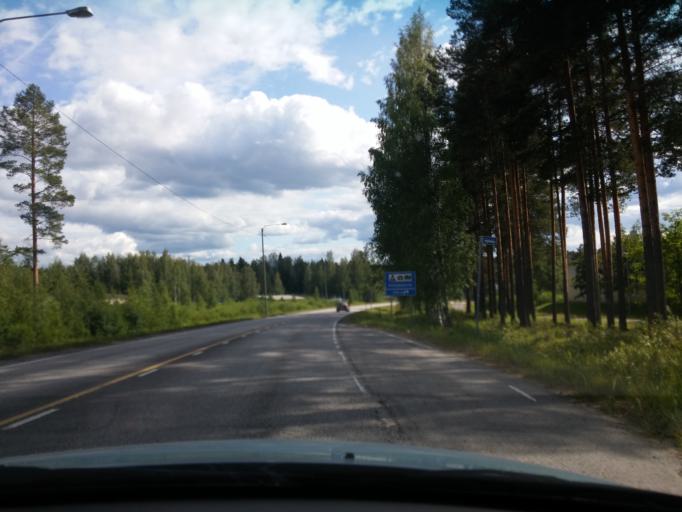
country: FI
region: Central Finland
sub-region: Keuruu
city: Keuruu
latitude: 62.2483
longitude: 24.7247
